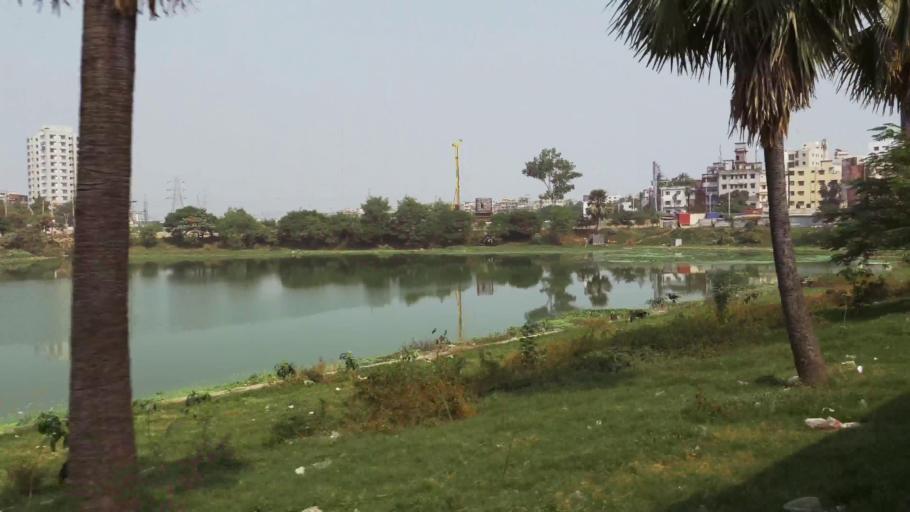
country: BD
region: Dhaka
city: Azimpur
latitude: 23.7547
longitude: 90.3943
